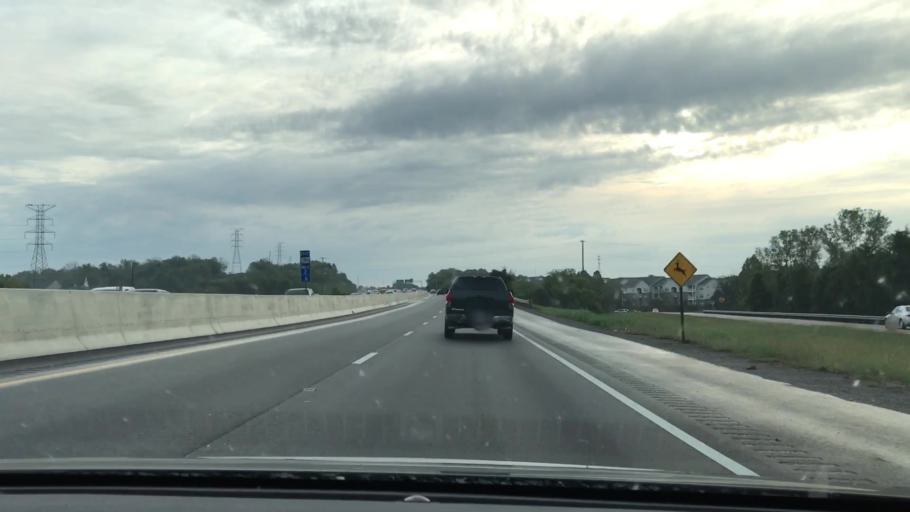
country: US
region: Tennessee
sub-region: Davidson County
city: Goodlettsville
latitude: 36.3123
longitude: -86.6685
